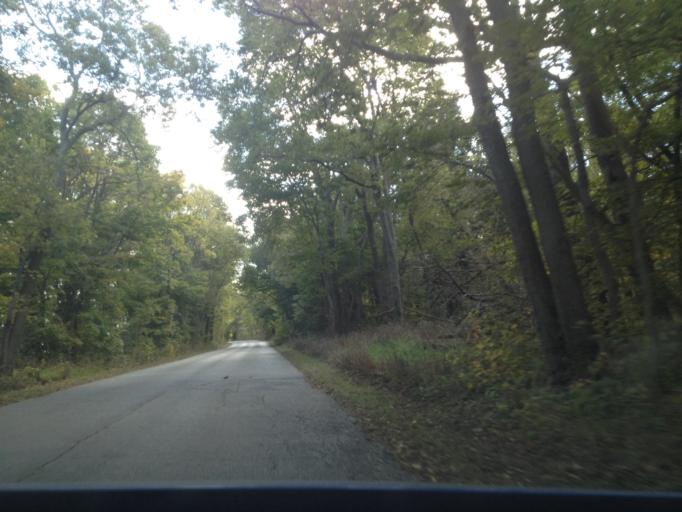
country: CA
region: Ontario
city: Amherstburg
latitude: 41.9798
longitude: -82.5422
